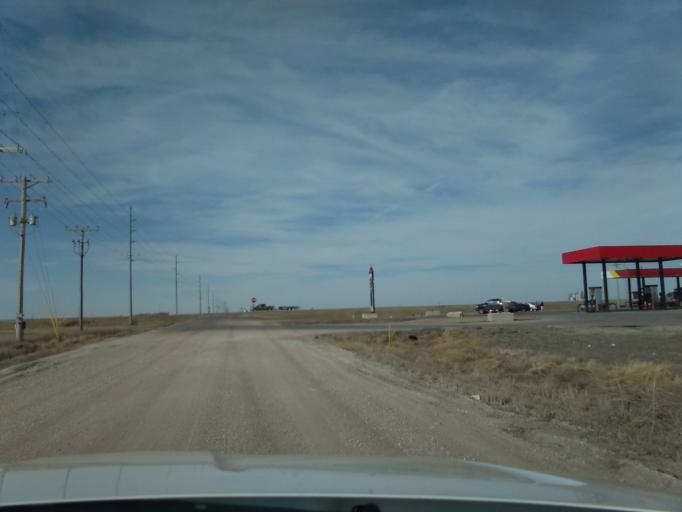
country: US
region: Nebraska
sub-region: Fillmore County
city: Geneva
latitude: 40.6258
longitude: -97.5940
